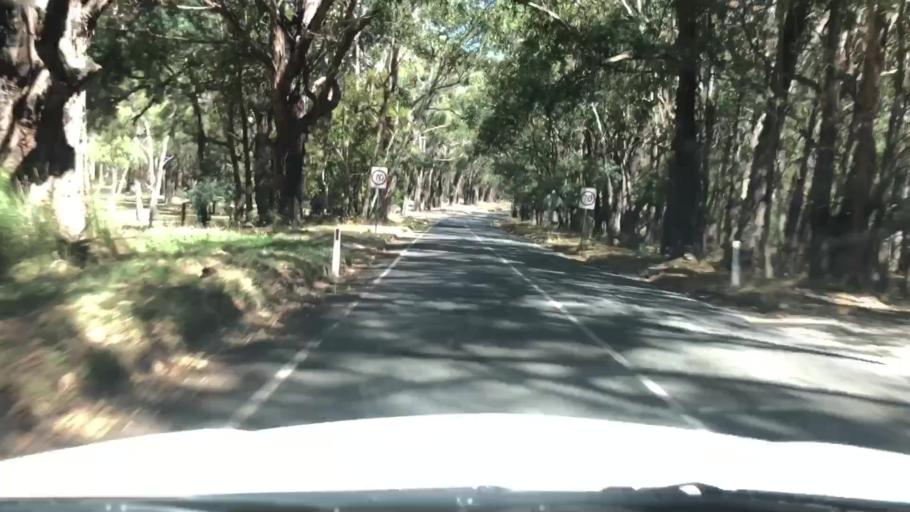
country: AU
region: Victoria
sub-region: Yarra Ranges
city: Macclesfield
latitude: -37.8343
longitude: 145.4874
